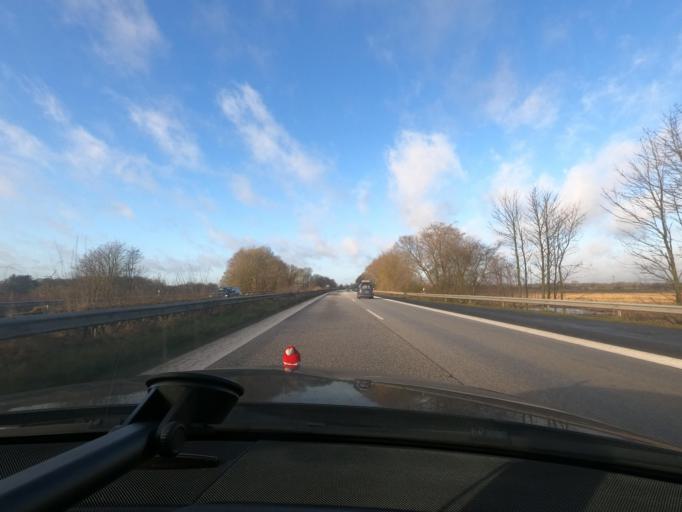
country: DE
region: Schleswig-Holstein
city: Brekendorf
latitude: 54.4164
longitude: 9.6107
